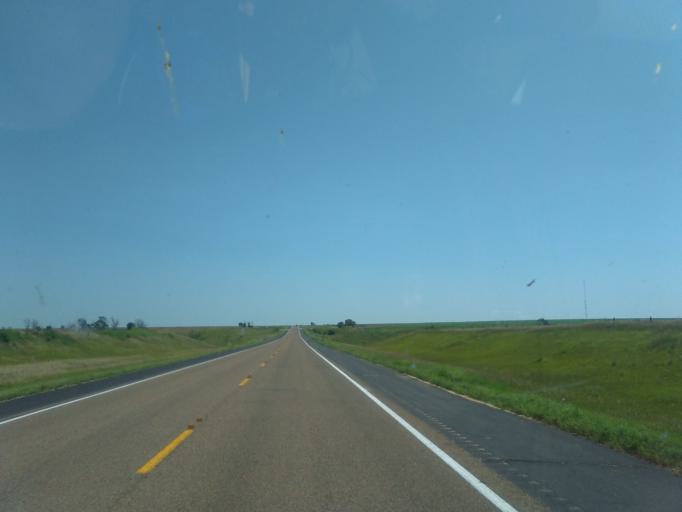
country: US
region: Nebraska
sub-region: Hitchcock County
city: Trenton
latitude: 40.2174
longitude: -100.9429
